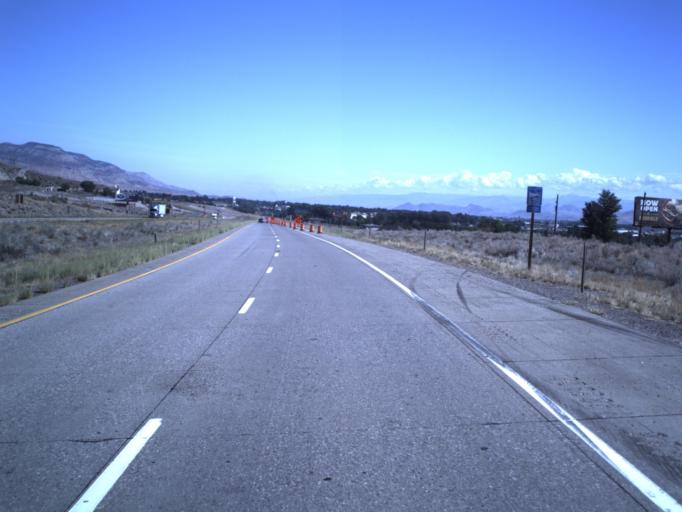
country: US
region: Utah
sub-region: Sevier County
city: Richfield
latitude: 38.7342
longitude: -112.1173
